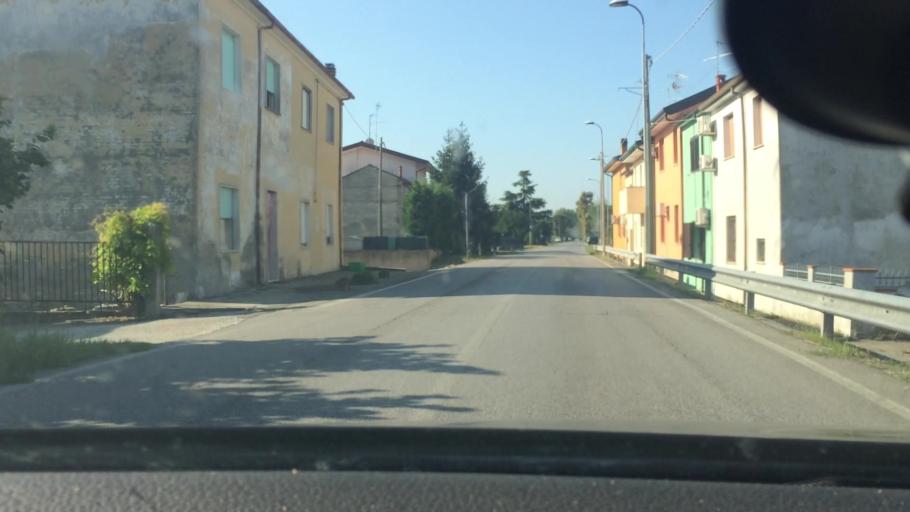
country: IT
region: Emilia-Romagna
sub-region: Provincia di Ferrara
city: Lagosanto
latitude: 44.7552
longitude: 12.1382
